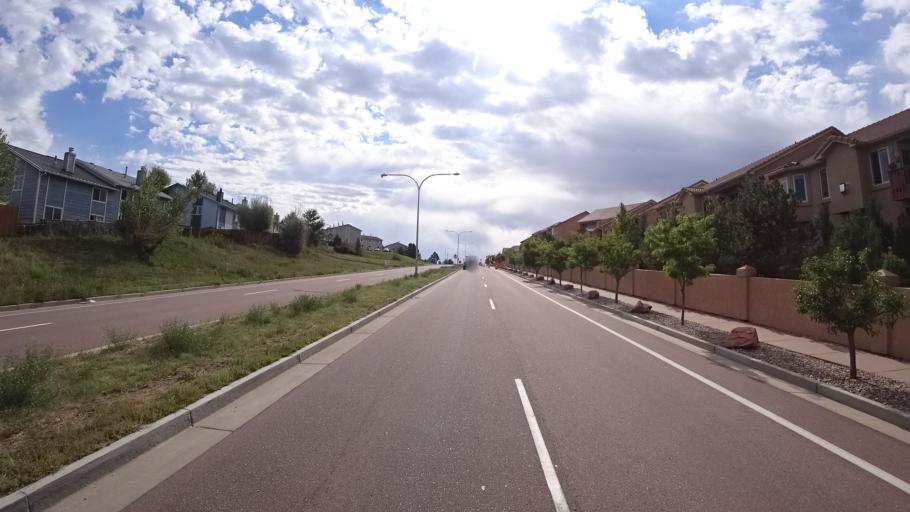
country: US
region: Colorado
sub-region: El Paso County
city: Cimarron Hills
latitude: 38.8948
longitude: -104.7299
